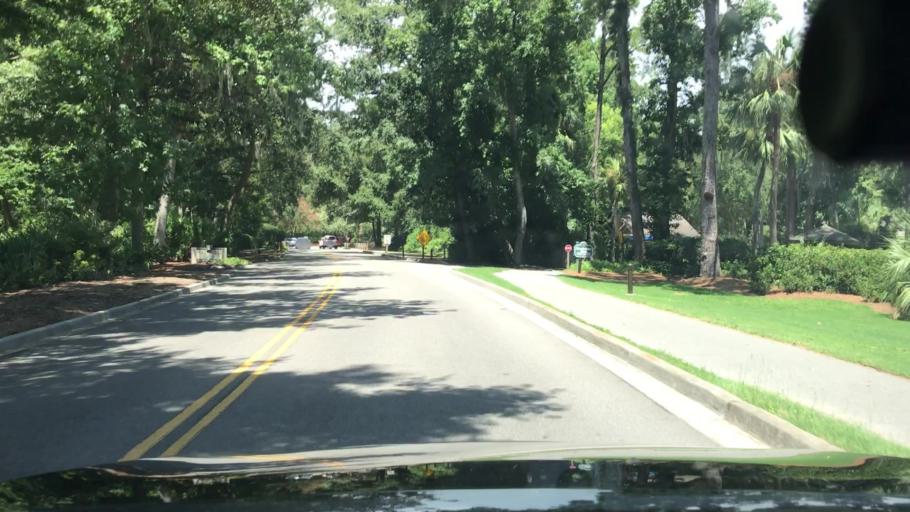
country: US
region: South Carolina
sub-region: Beaufort County
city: Hilton Head Island
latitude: 32.1306
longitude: -80.7942
